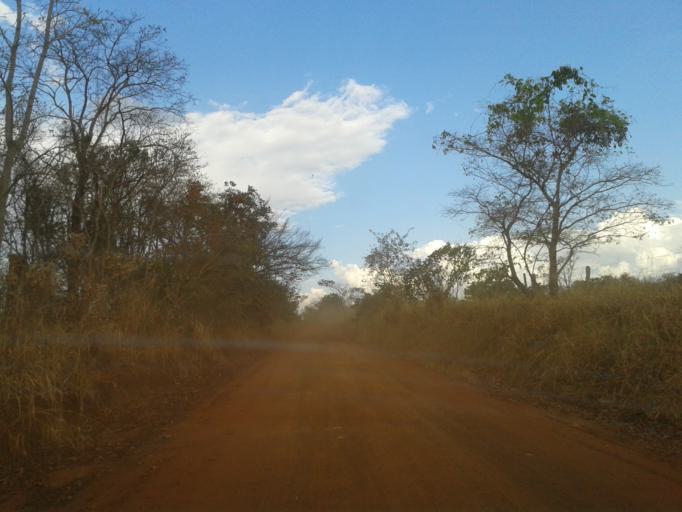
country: BR
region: Minas Gerais
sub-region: Santa Vitoria
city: Santa Vitoria
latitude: -19.1970
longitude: -49.9133
